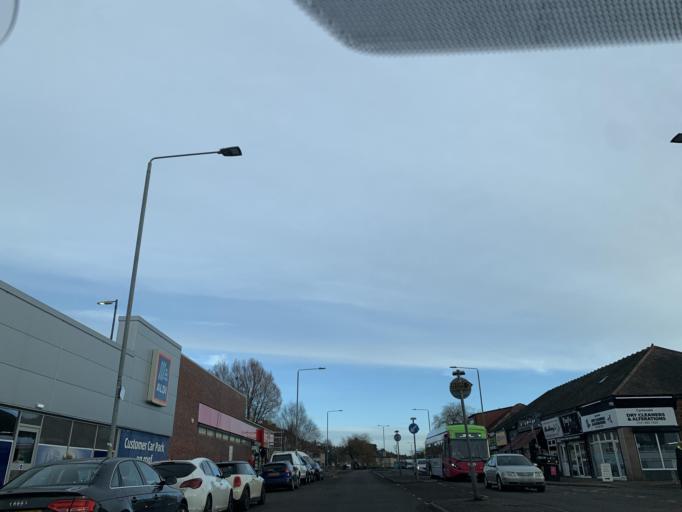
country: GB
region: Scotland
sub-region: Renfrewshire
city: Renfrew
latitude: 55.8459
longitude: -4.3545
